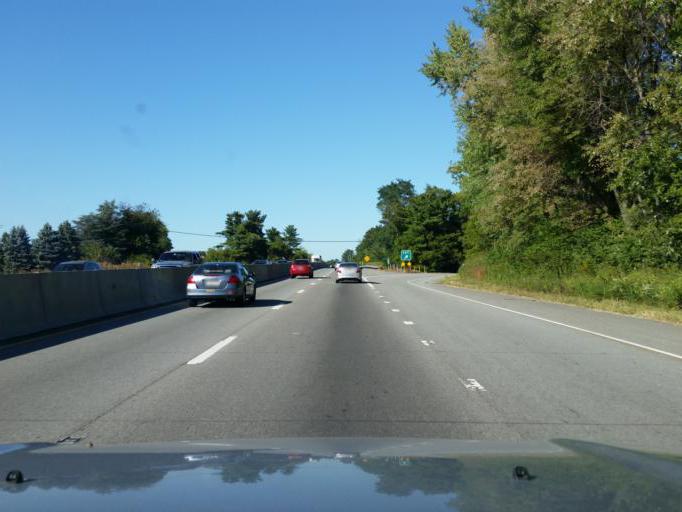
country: US
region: Pennsylvania
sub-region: Chester County
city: West Chester
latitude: 39.9535
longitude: -75.5812
